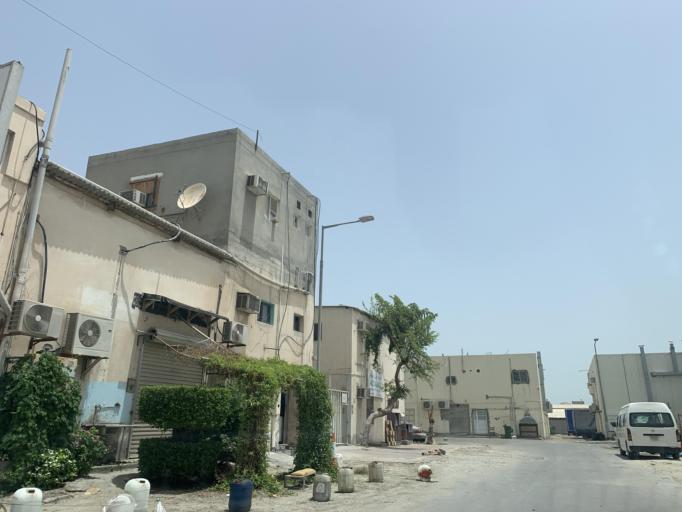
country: BH
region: Northern
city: Ar Rifa'
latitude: 26.1377
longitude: 50.5878
